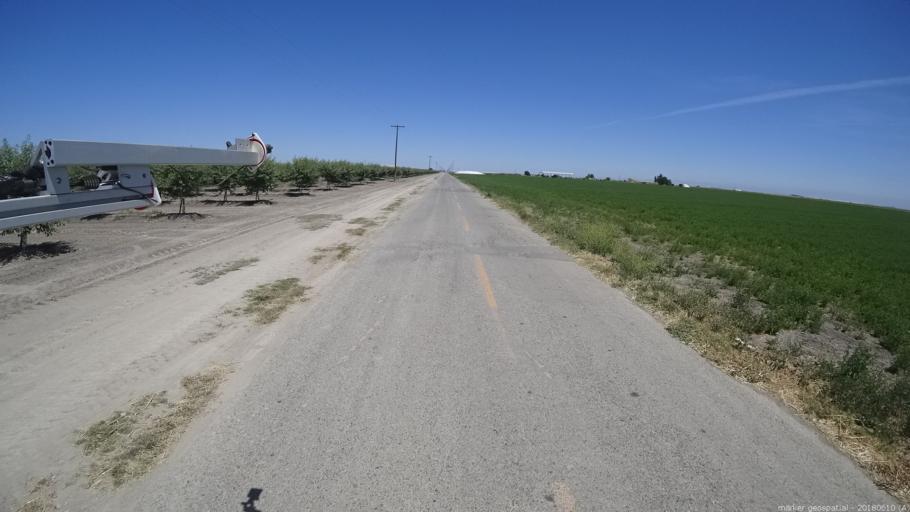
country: US
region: California
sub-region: Merced County
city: Dos Palos
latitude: 37.0349
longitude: -120.5287
